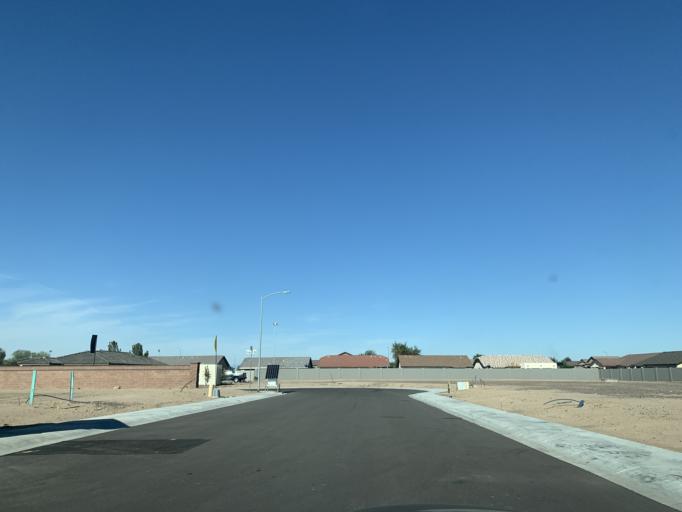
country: US
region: Arizona
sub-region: Maricopa County
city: Laveen
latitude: 33.3950
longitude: -112.1244
